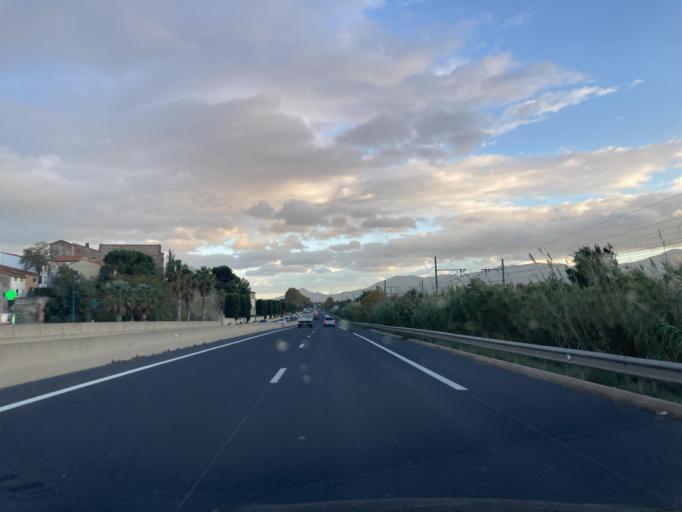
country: FR
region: Languedoc-Roussillon
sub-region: Departement des Pyrenees-Orientales
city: Corneilla-del-Vercol
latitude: 42.6266
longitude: 2.9469
